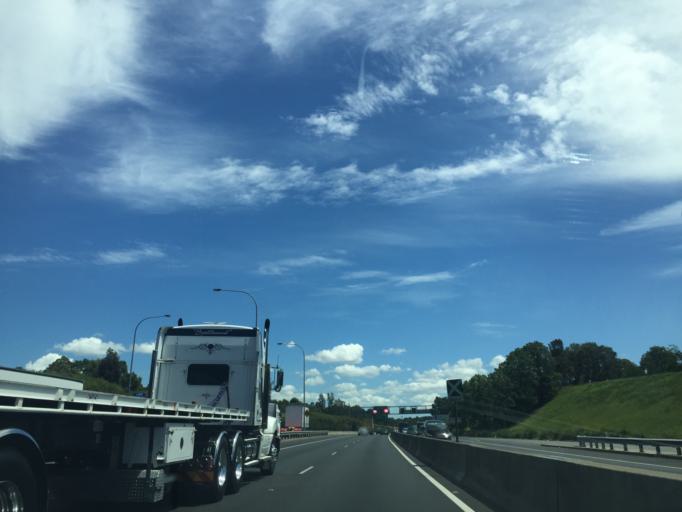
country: AU
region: New South Wales
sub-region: Canterbury
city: Clemton Park
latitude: -33.9403
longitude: 151.0932
